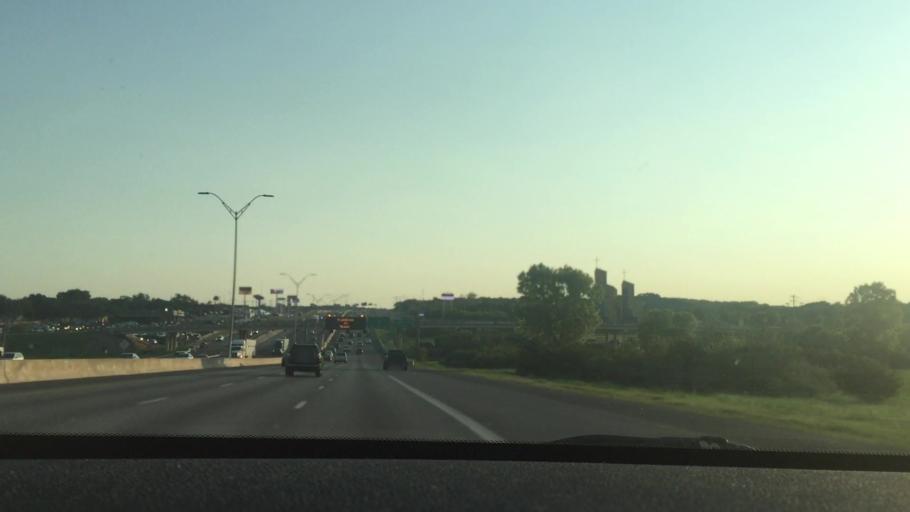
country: US
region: Texas
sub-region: Bexar County
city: Live Oak
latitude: 29.5627
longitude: -98.3394
